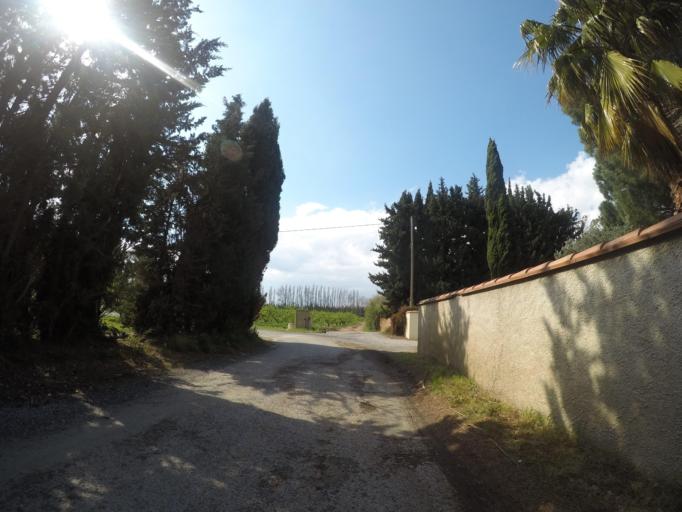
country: FR
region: Languedoc-Roussillon
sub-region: Departement des Pyrenees-Orientales
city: Pezilla-la-Riviere
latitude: 42.6697
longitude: 2.7683
